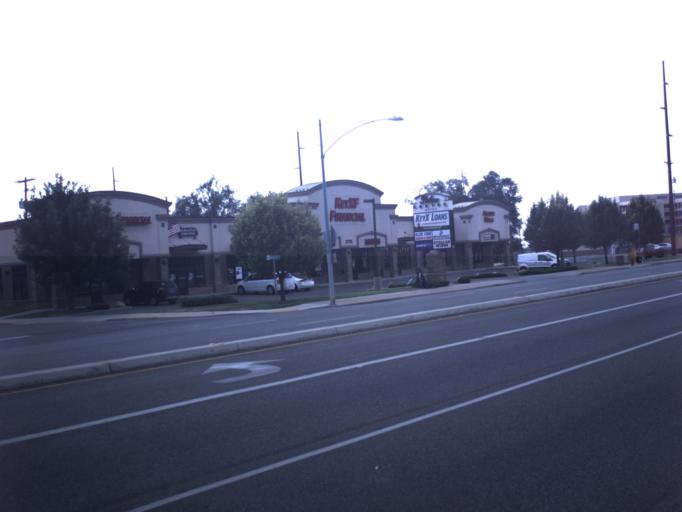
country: US
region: Utah
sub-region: Salt Lake County
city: South Salt Lake
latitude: 40.7116
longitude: -111.8881
